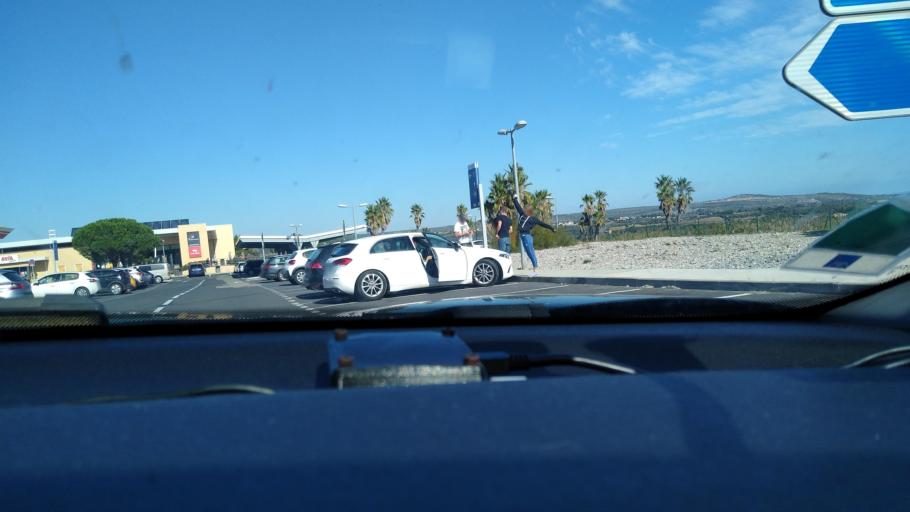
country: FR
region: Languedoc-Roussillon
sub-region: Departement de l'Aude
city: Leucate
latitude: 42.9508
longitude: 2.9721
